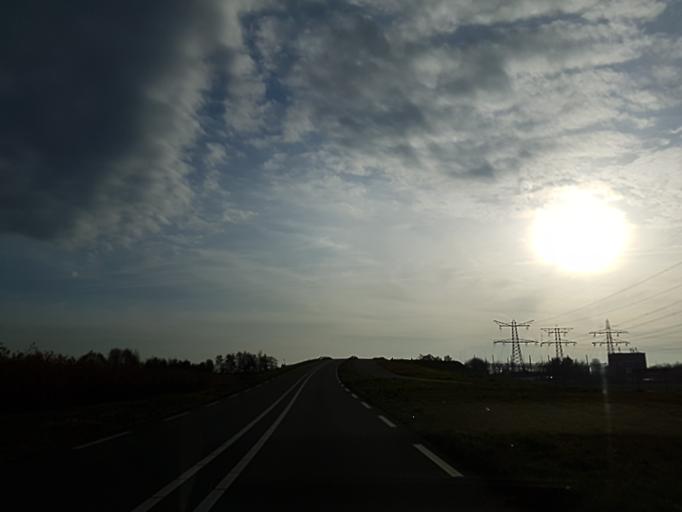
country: NL
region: North Brabant
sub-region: Roosendaal
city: Roosendaal
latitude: 51.5501
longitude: 4.4873
